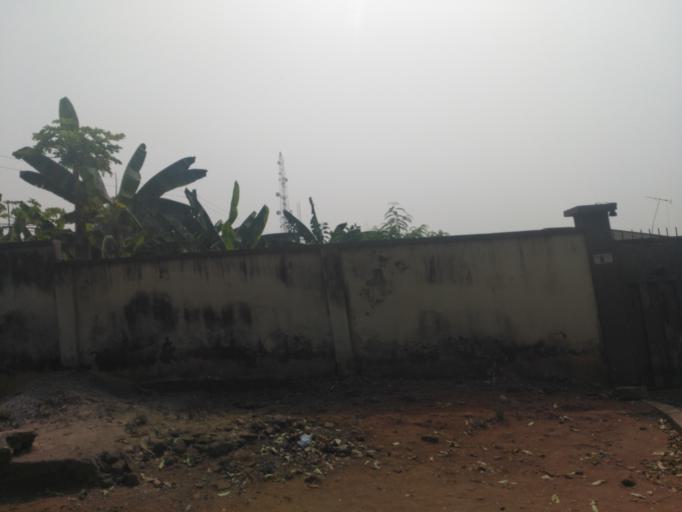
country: GH
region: Ashanti
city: Kumasi
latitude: 6.6763
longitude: -1.6204
